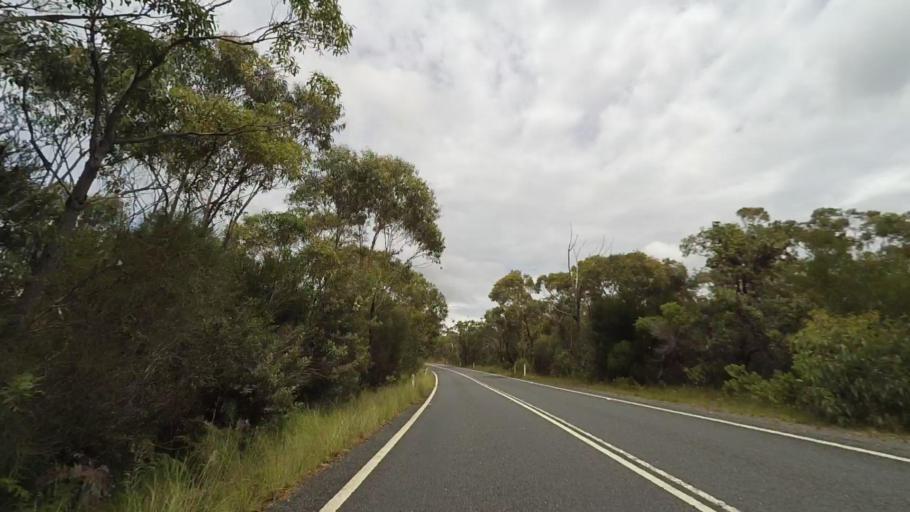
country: AU
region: New South Wales
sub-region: Sutherland Shire
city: Heathcote
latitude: -34.0998
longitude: 151.0589
